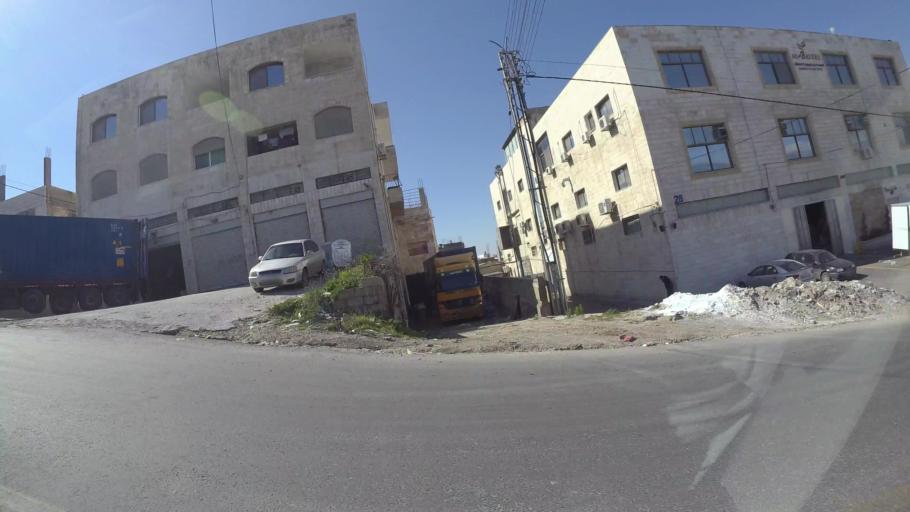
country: JO
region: Amman
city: Al Bunayyat ash Shamaliyah
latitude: 31.9129
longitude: 35.9070
